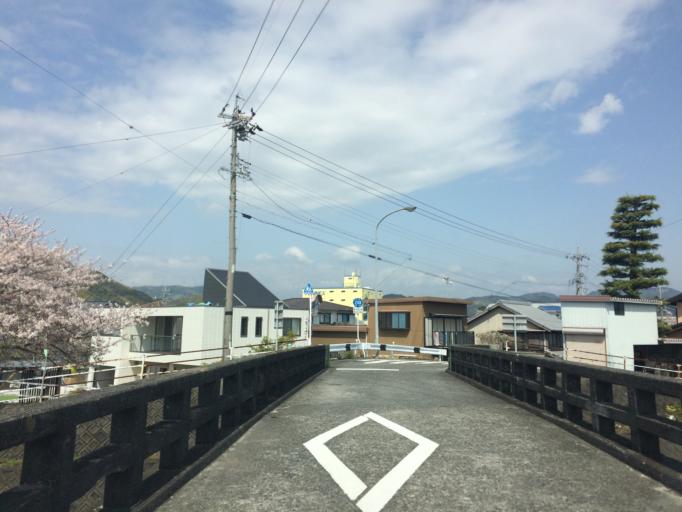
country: JP
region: Shizuoka
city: Fujieda
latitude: 34.8861
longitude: 138.2806
